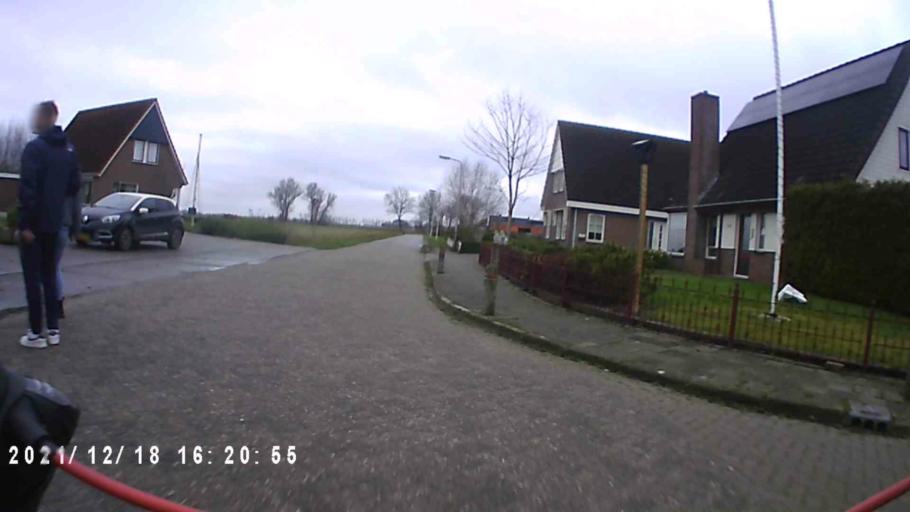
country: NL
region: Friesland
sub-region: Gemeente Dongeradeel
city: Dokkum
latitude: 53.3791
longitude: 6.0489
